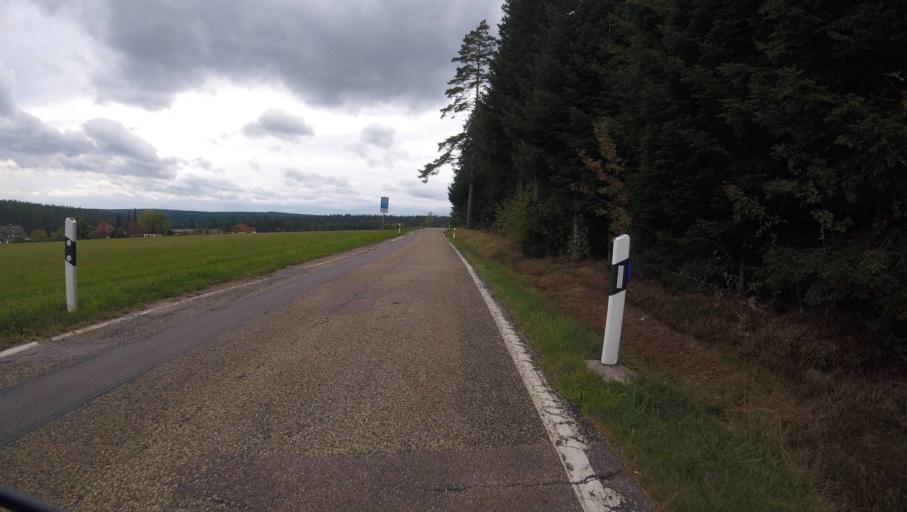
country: DE
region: Baden-Wuerttemberg
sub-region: Karlsruhe Region
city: Simmersfeld
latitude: 48.6021
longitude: 8.4486
